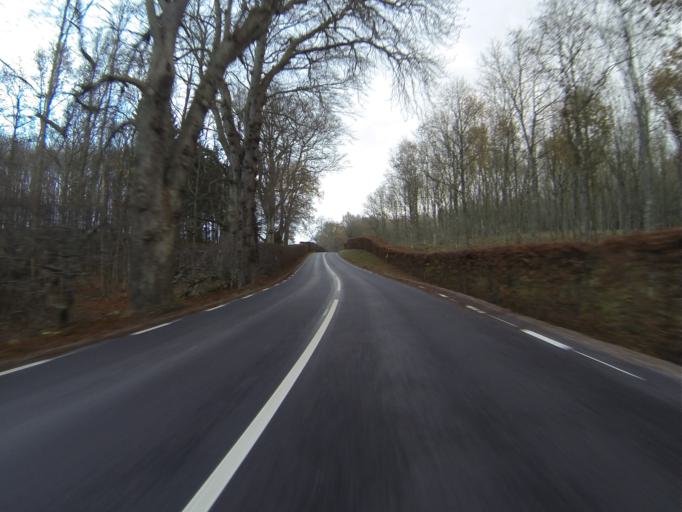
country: SE
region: Skane
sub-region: Lunds Kommun
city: Genarp
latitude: 55.5864
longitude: 13.4204
